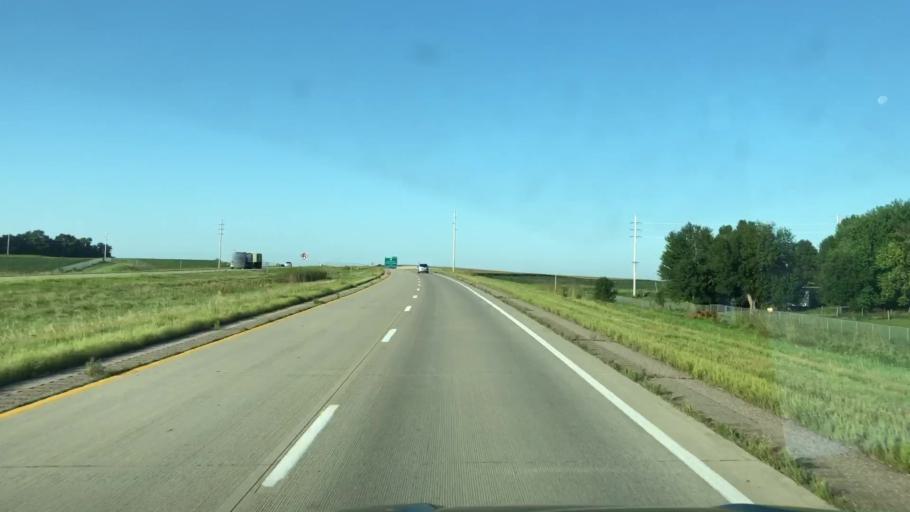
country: US
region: Iowa
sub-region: Plymouth County
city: Le Mars
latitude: 42.8139
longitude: -96.1915
